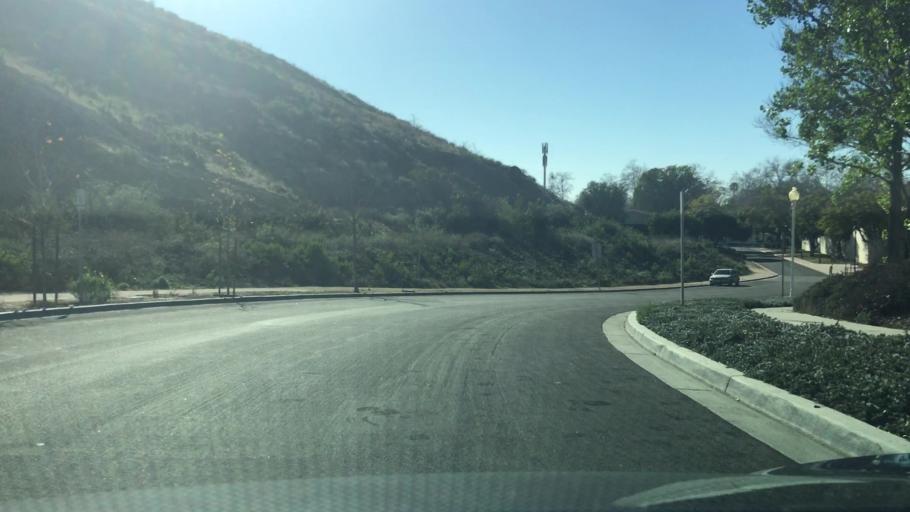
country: US
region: California
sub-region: Ventura County
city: Camarillo
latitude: 34.1620
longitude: -119.0387
